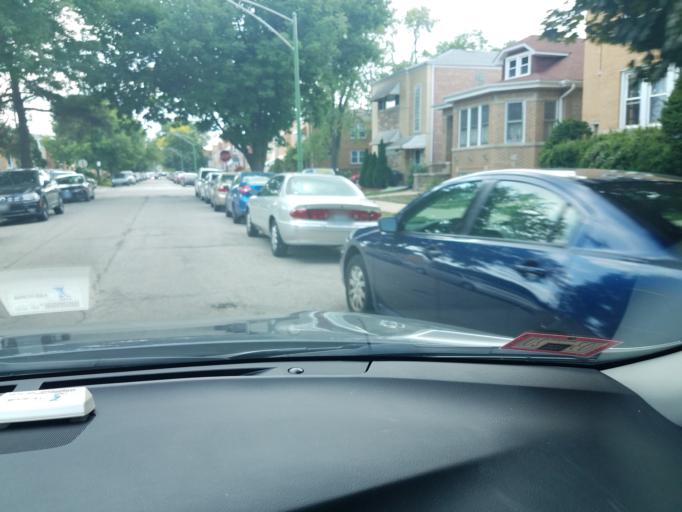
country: US
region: Illinois
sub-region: Cook County
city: Harwood Heights
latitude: 41.9834
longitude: -87.7720
